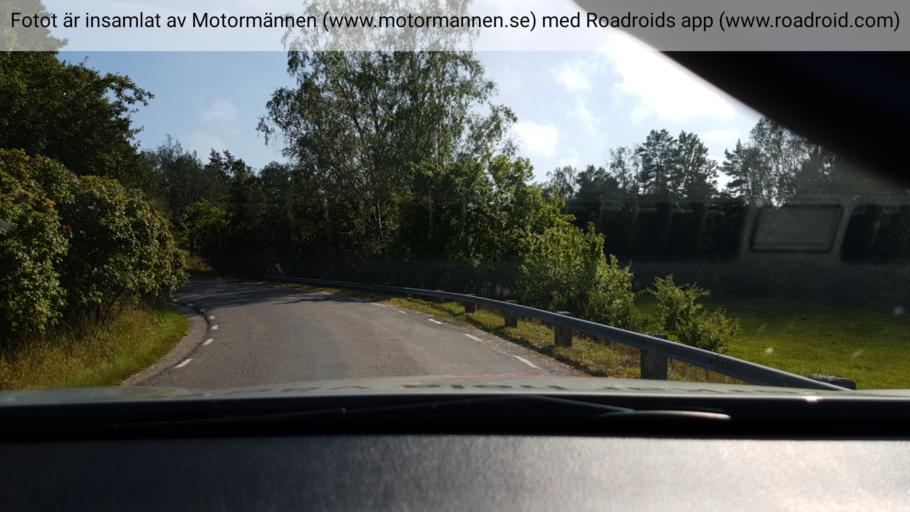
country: SE
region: Stockholm
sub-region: Nynashamns Kommun
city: Osmo
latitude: 58.8845
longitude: 17.7884
